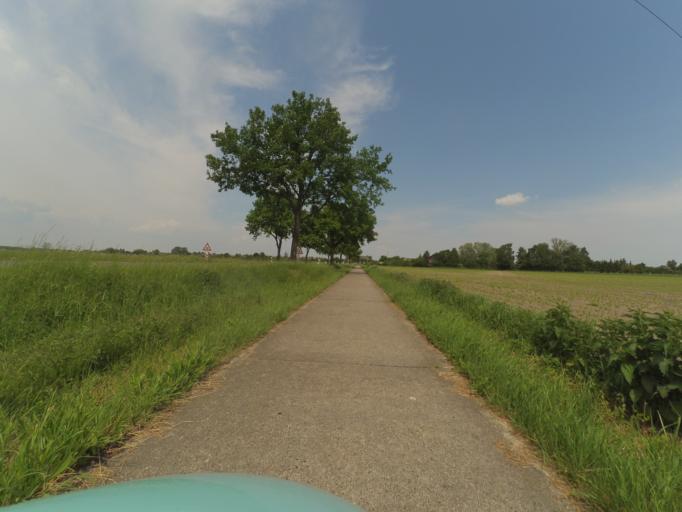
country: DE
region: Lower Saxony
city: Peine
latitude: 52.3312
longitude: 10.1741
